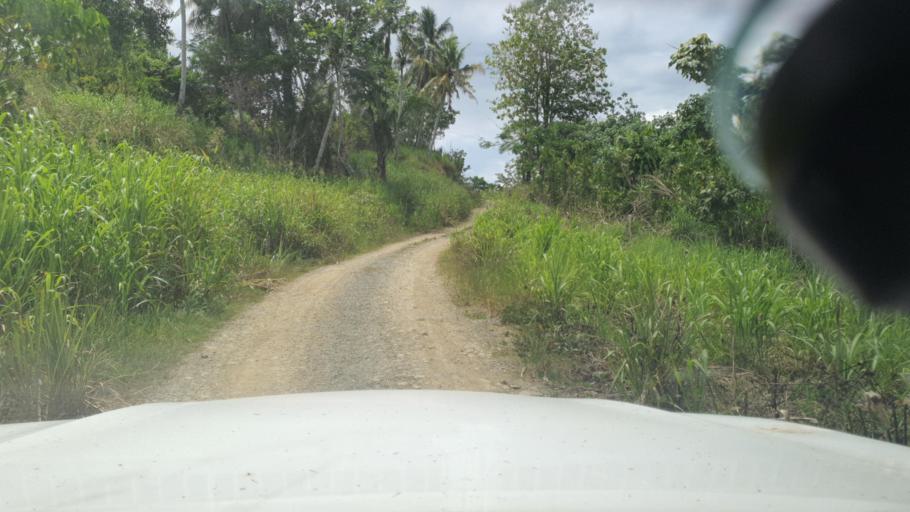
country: SB
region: Guadalcanal
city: Honiara
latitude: -9.4847
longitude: 160.3363
